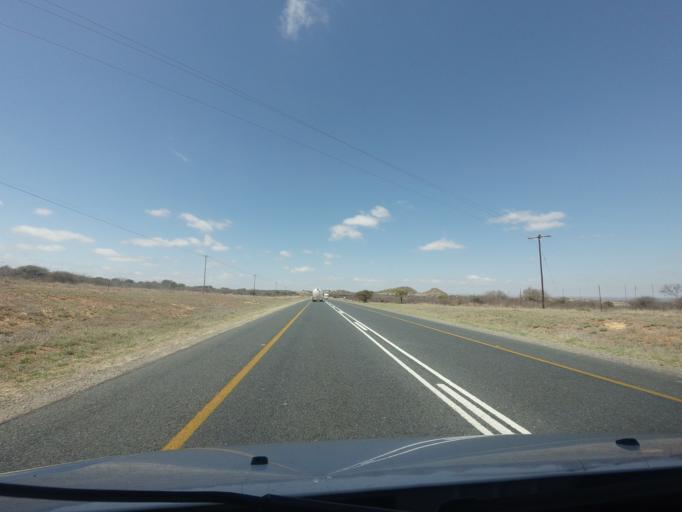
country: ZA
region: Limpopo
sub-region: Vhembe District Municipality
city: Louis Trichardt
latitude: -23.4240
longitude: 29.7504
